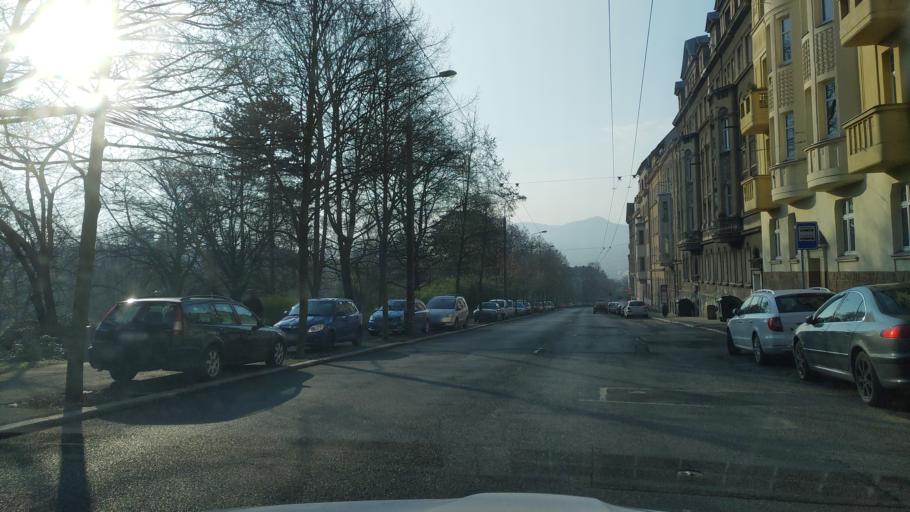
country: CZ
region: Ustecky
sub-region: Okres Usti nad Labem
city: Usti nad Labem
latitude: 50.6674
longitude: 14.0247
